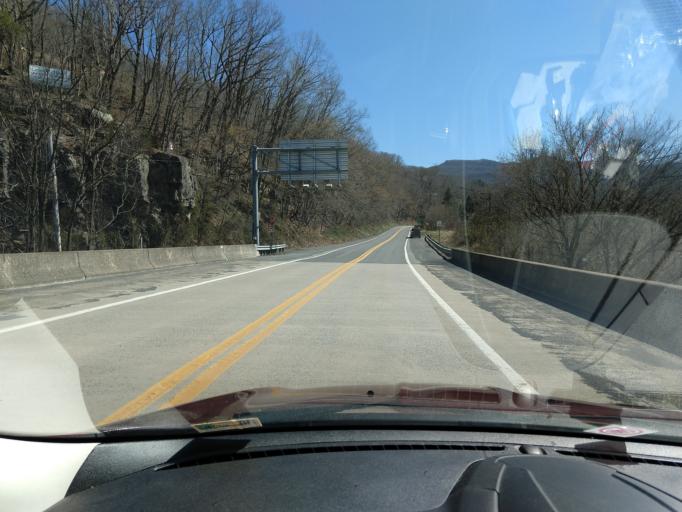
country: US
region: West Virginia
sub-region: Summers County
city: Hinton
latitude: 37.7789
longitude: -80.8926
